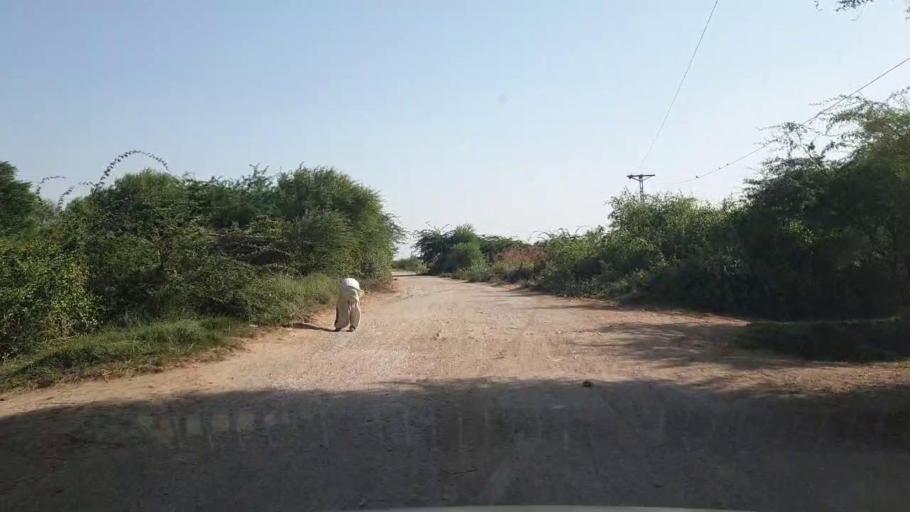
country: PK
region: Sindh
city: Matli
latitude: 25.0552
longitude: 68.7196
